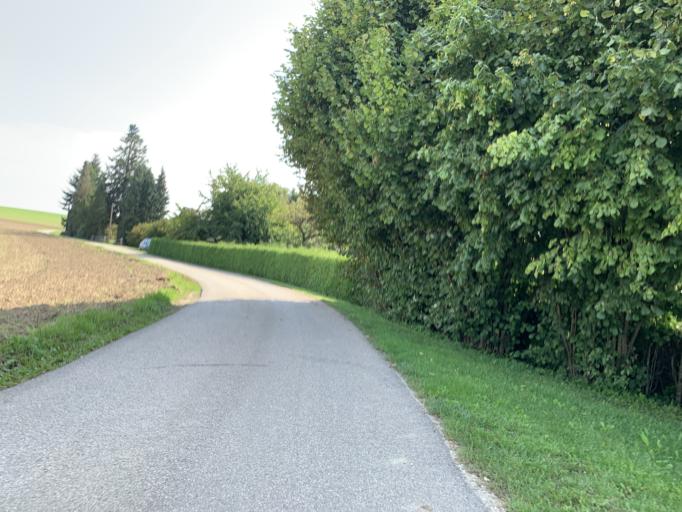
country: DE
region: Bavaria
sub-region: Upper Bavaria
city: Marzling
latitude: 48.4194
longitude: 11.8189
